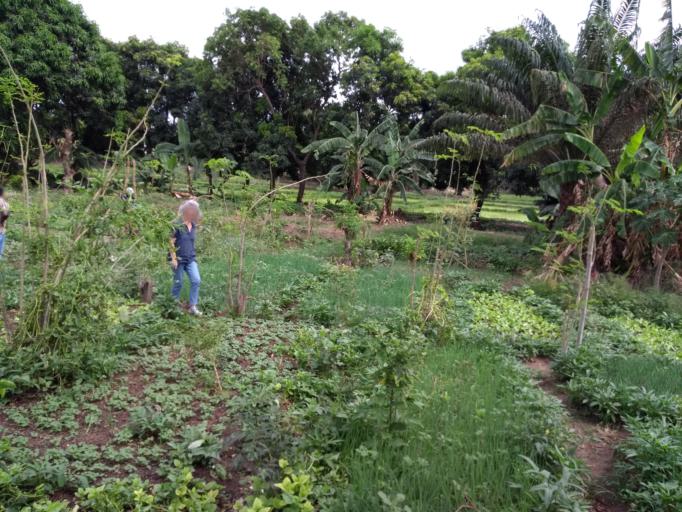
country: CI
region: Vallee du Bandama
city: Bouake
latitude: 7.7066
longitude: -5.0382
